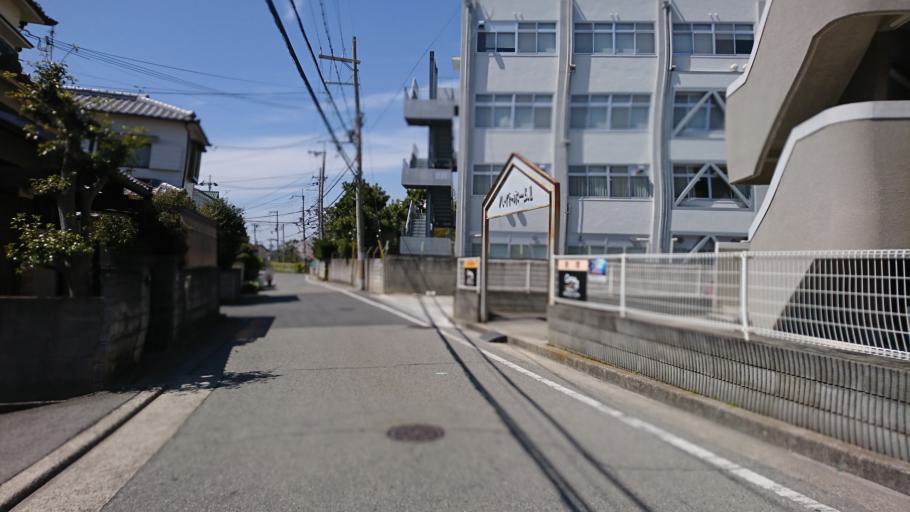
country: JP
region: Hyogo
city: Kakogawacho-honmachi
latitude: 34.7460
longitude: 134.8829
